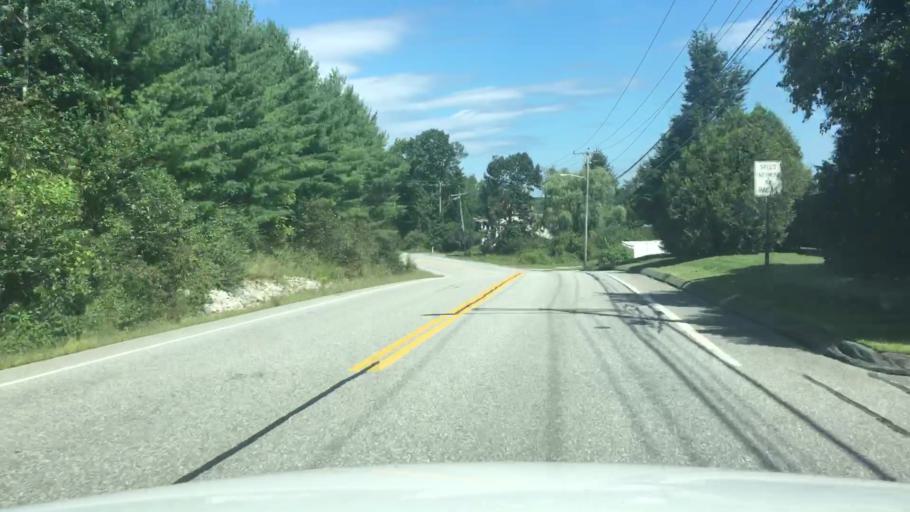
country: US
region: Maine
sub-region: Androscoggin County
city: Lewiston
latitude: 44.1297
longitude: -70.2275
